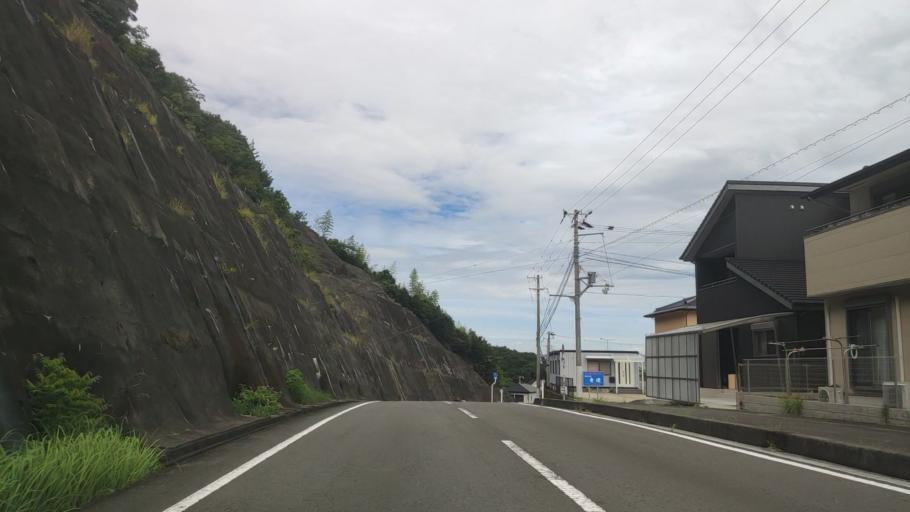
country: JP
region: Wakayama
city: Tanabe
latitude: 33.6879
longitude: 135.3886
